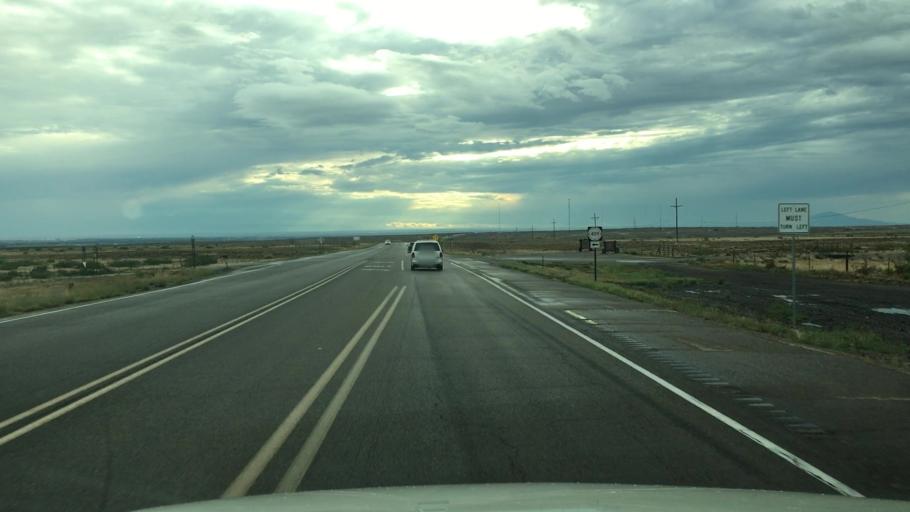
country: US
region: New Mexico
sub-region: Chaves County
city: Roswell
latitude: 33.3995
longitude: -104.3454
